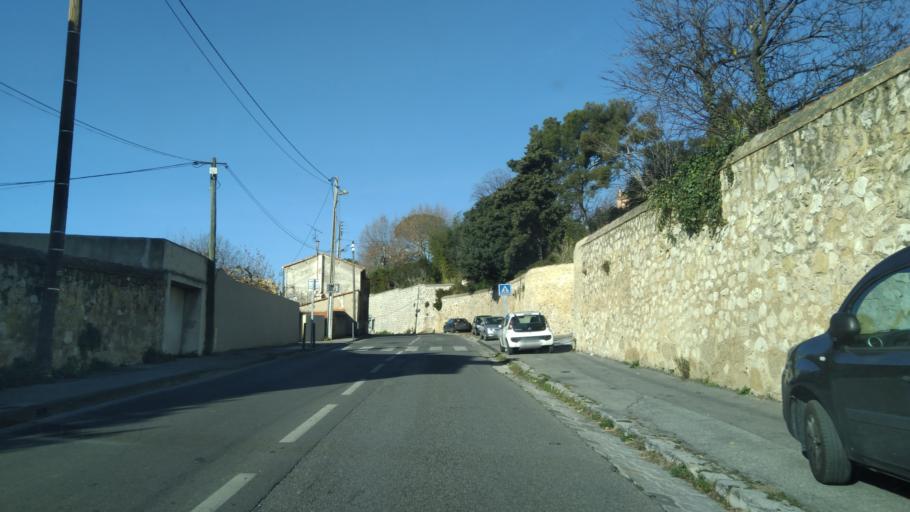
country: FR
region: Provence-Alpes-Cote d'Azur
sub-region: Departement des Bouches-du-Rhone
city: Marseille 12
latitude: 43.3028
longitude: 5.4432
